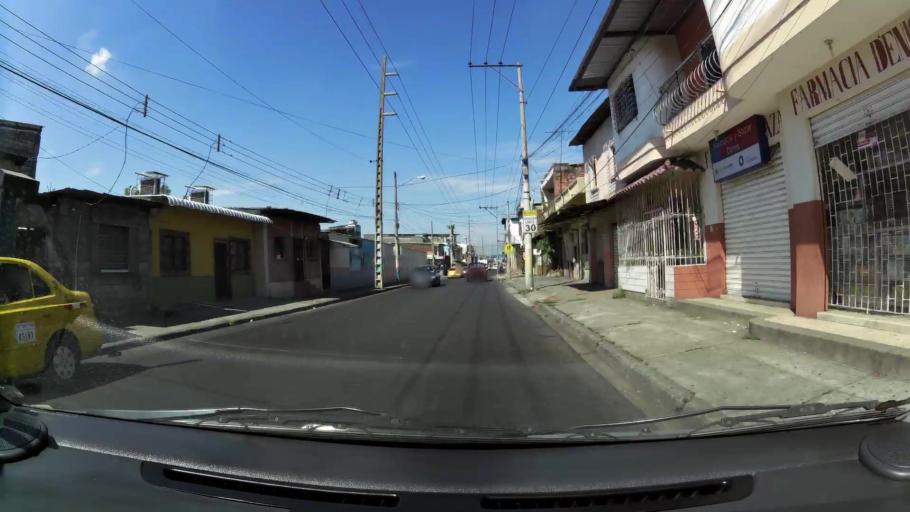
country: EC
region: Guayas
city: Guayaquil
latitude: -2.2087
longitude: -79.9209
